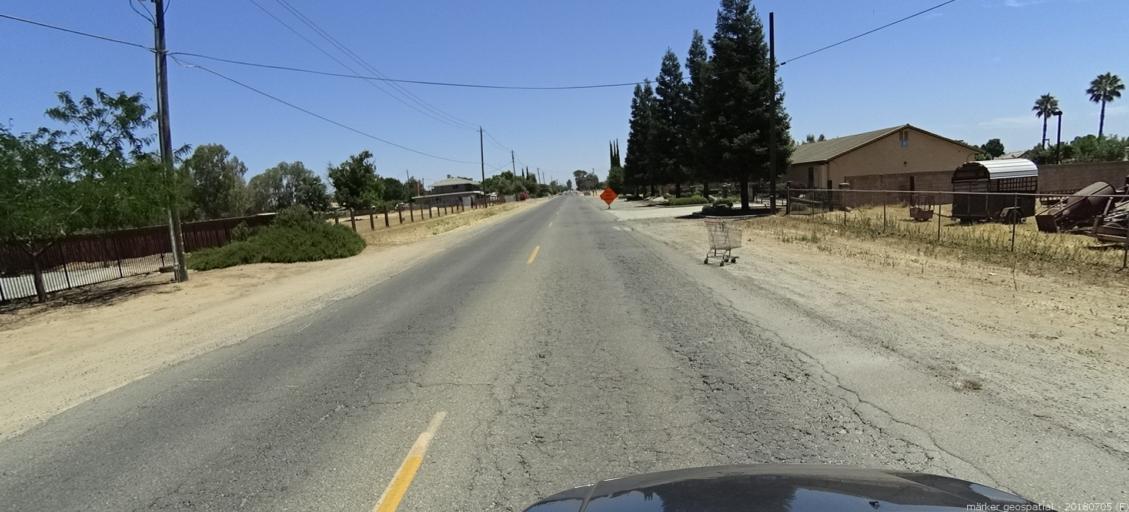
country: US
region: California
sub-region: Madera County
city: Madera
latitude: 36.9869
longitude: -120.0687
